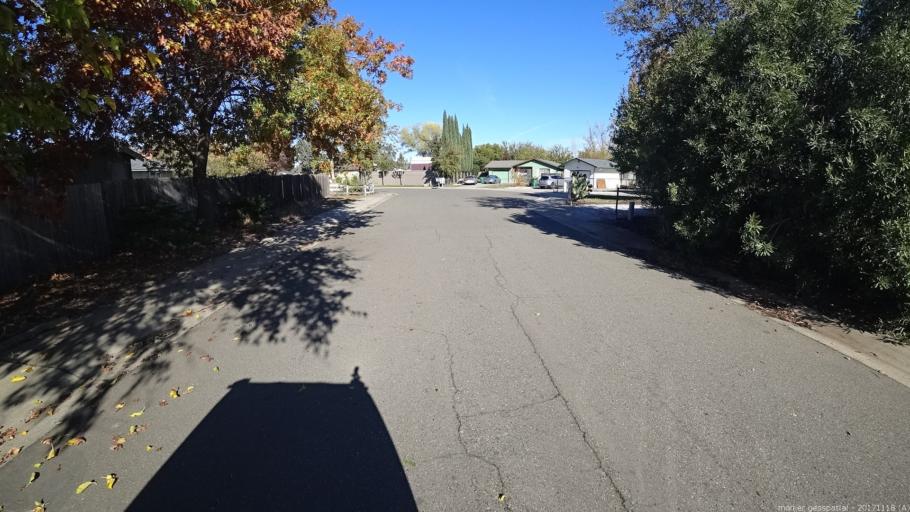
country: US
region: California
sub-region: Shasta County
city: Cottonwood
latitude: 40.3939
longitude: -122.2757
